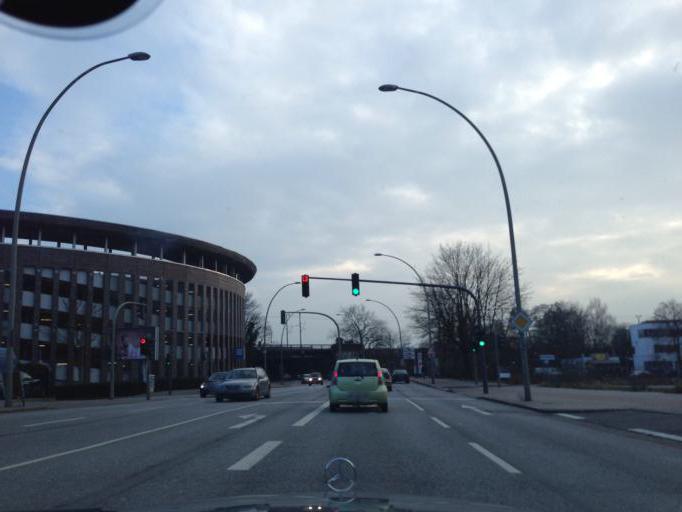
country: DE
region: Hamburg
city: Bergedorf
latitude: 53.4901
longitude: 10.2033
